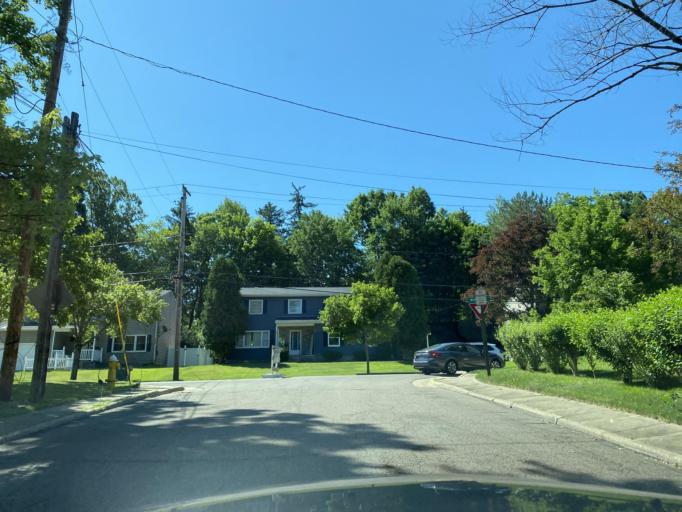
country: US
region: Ohio
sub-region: Summit County
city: Fairlawn
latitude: 41.1214
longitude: -81.5560
